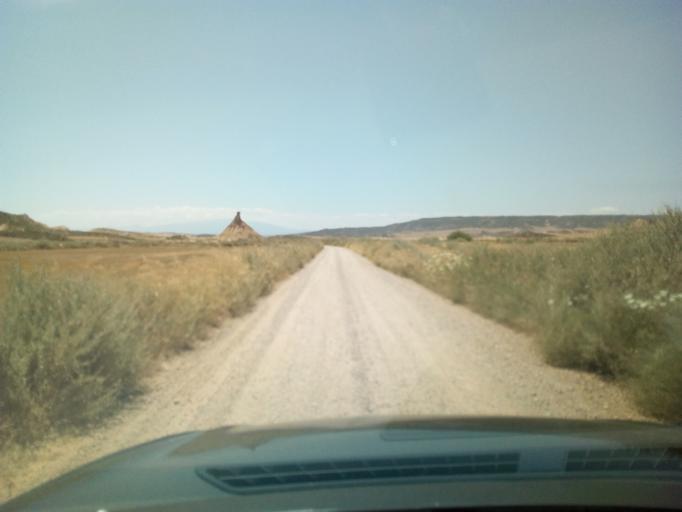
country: ES
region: Navarre
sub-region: Provincia de Navarra
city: Arguedas
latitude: 42.2156
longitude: -1.5117
